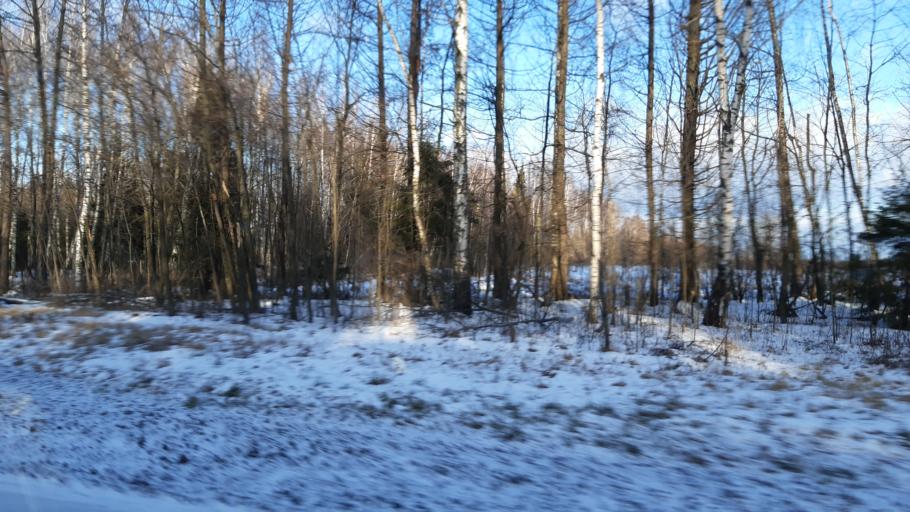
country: RU
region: Vladimir
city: Arsaki
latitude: 56.2630
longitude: 38.4332
